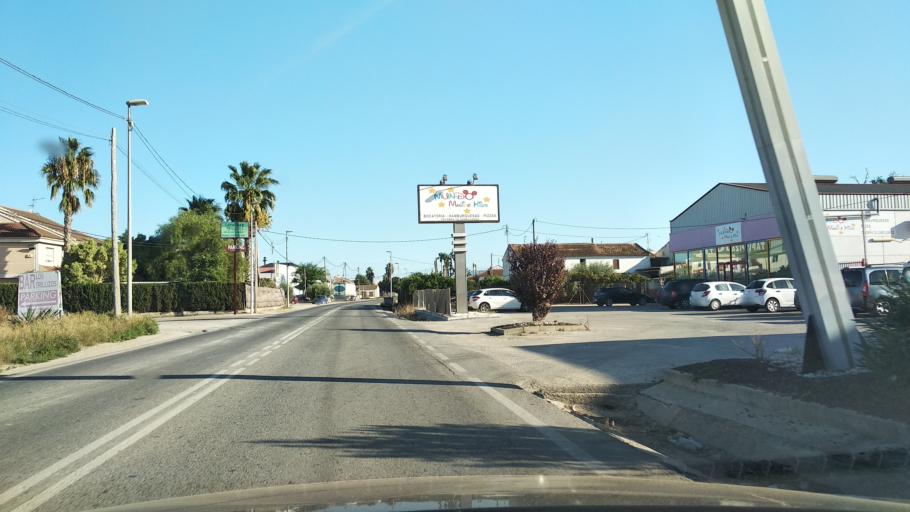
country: ES
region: Murcia
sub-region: Murcia
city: Santomera
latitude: 38.0427
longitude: -1.0507
